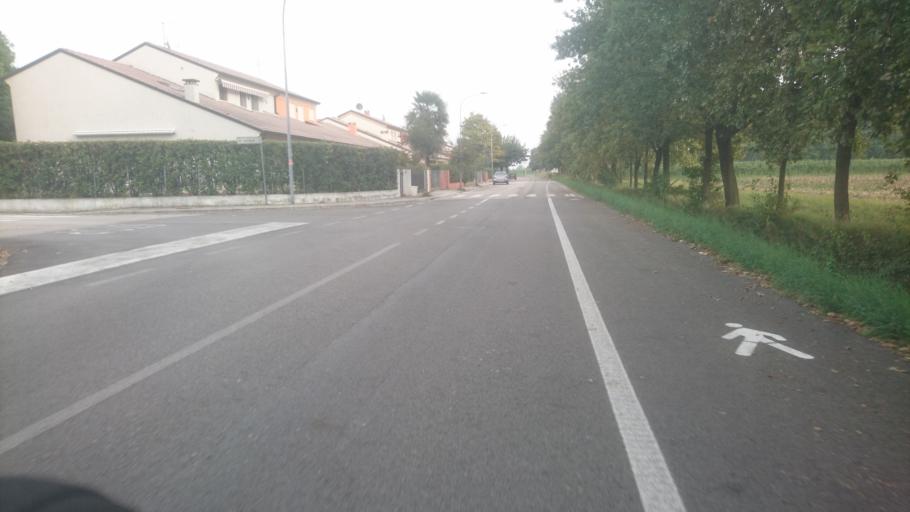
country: IT
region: Veneto
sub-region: Provincia di Vicenza
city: Montegalda
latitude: 45.4470
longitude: 11.6836
